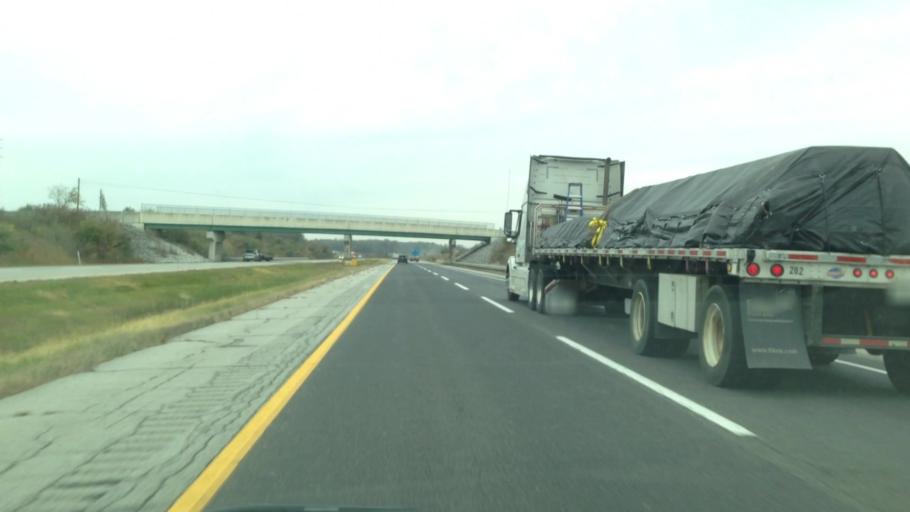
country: US
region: Indiana
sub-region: Steuben County
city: Fremont
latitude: 41.6799
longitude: -84.8765
